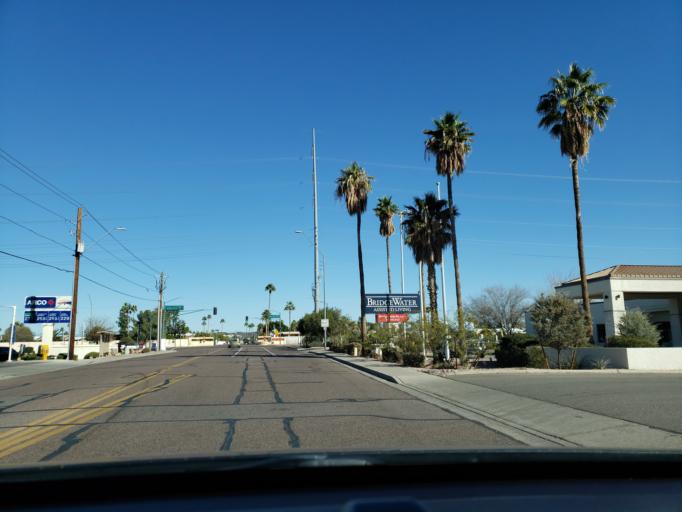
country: US
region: Arizona
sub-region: Maricopa County
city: Glendale
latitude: 33.6537
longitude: -112.1171
